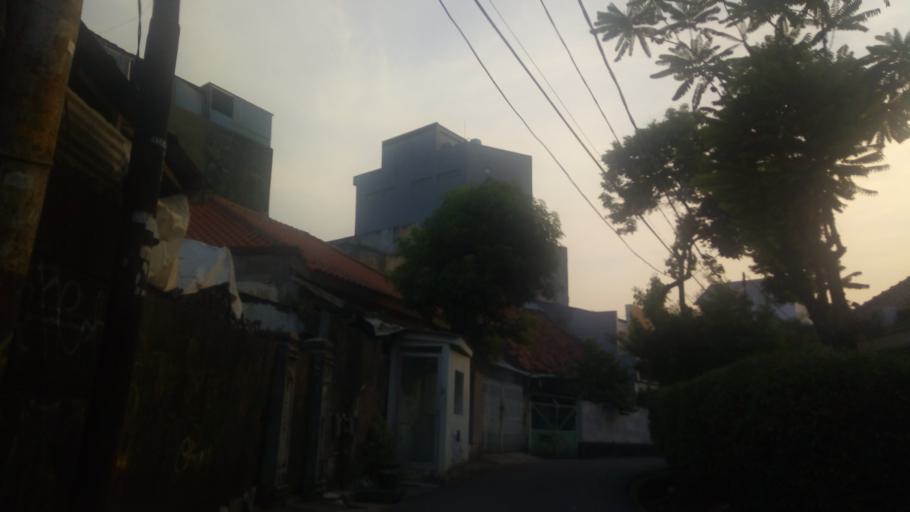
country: ID
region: Jakarta Raya
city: Jakarta
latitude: -6.2020
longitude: 106.8494
